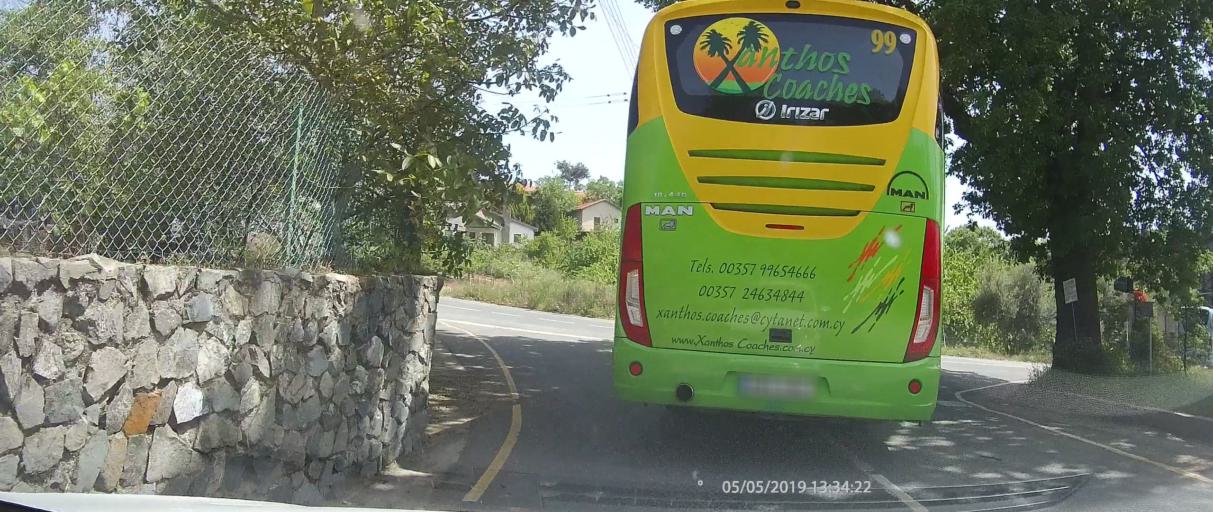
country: CY
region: Limassol
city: Pelendri
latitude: 34.8827
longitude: 32.8600
